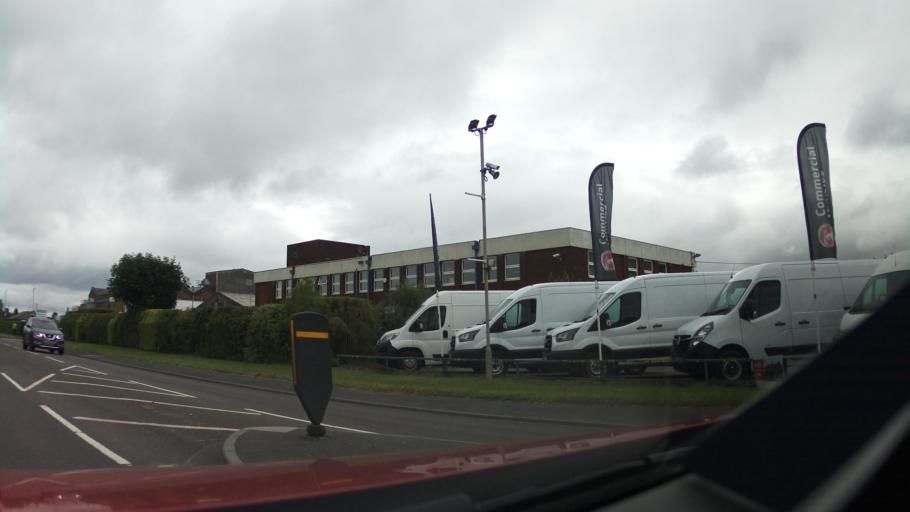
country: GB
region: England
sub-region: Staffordshire
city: Burton upon Trent
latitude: 52.8236
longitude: -1.6228
